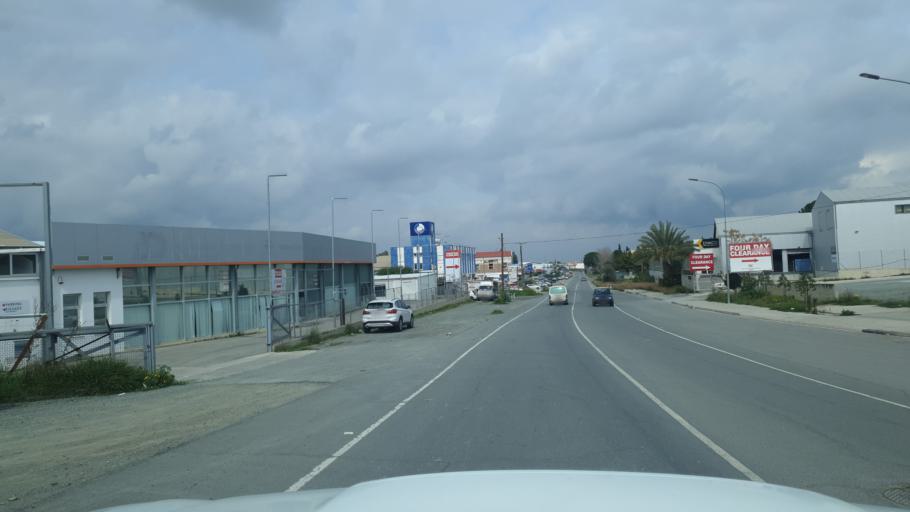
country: CY
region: Lefkosia
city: Geri
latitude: 35.0863
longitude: 33.3798
